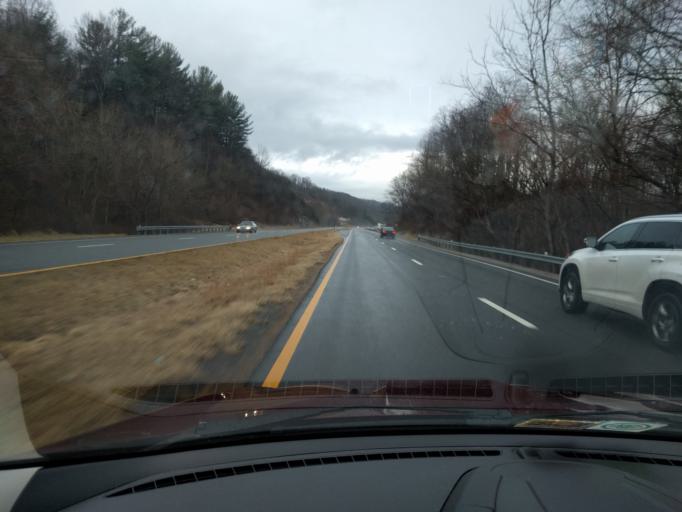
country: US
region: Virginia
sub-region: Montgomery County
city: Prices Fork
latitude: 37.3050
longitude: -80.5229
